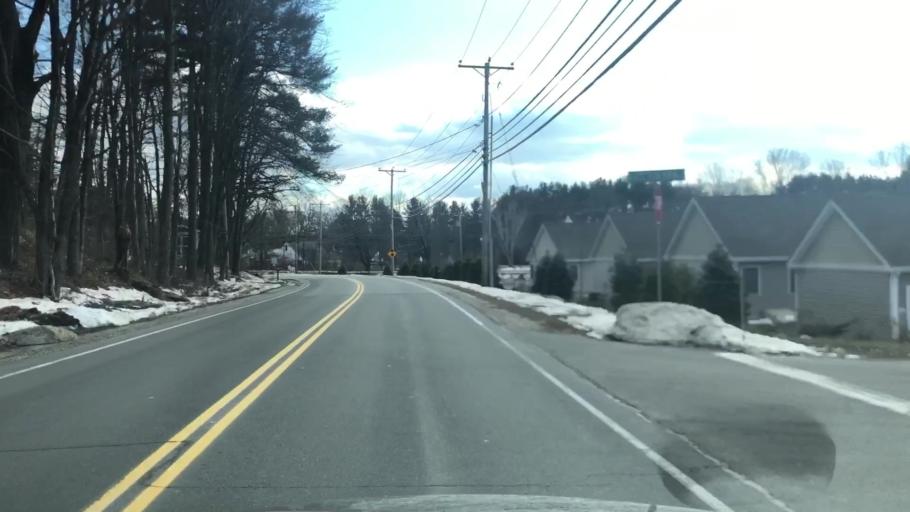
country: US
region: New Hampshire
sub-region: Hillsborough County
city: Milford
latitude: 42.8424
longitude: -71.6589
